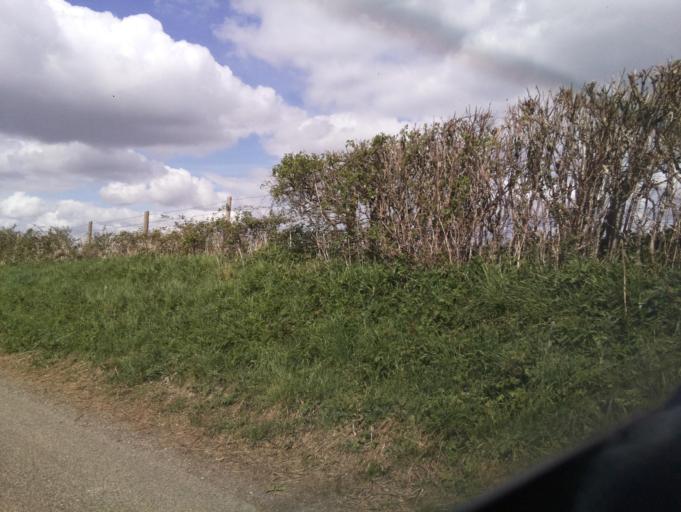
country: GB
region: England
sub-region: West Berkshire
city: Kintbury
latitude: 51.3684
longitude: -1.4779
